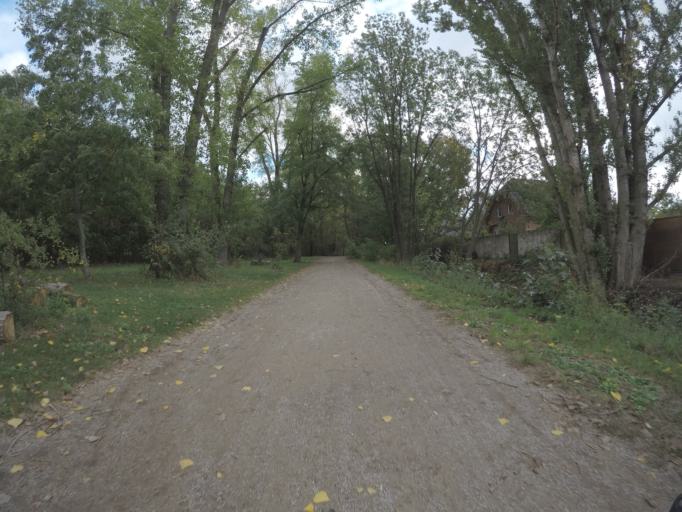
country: DE
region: Berlin
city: Stadtrandsiedlung Malchow
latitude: 52.5642
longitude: 13.4866
